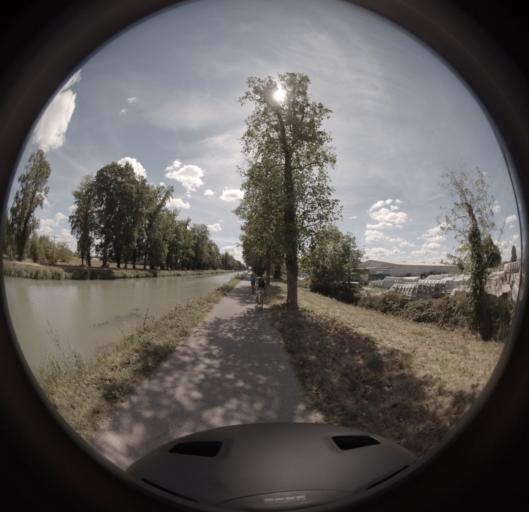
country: FR
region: Midi-Pyrenees
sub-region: Departement du Tarn-et-Garonne
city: Castelsarrasin
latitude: 44.0621
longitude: 1.1028
